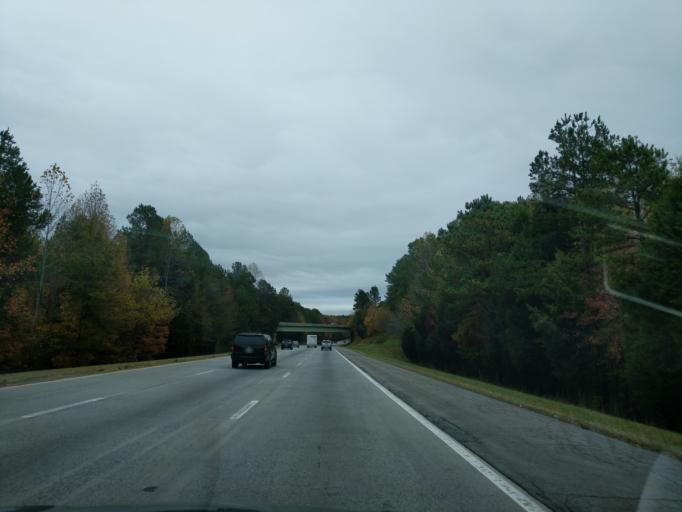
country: US
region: North Carolina
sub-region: Davidson County
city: Lexington
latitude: 35.8263
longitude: -80.1635
